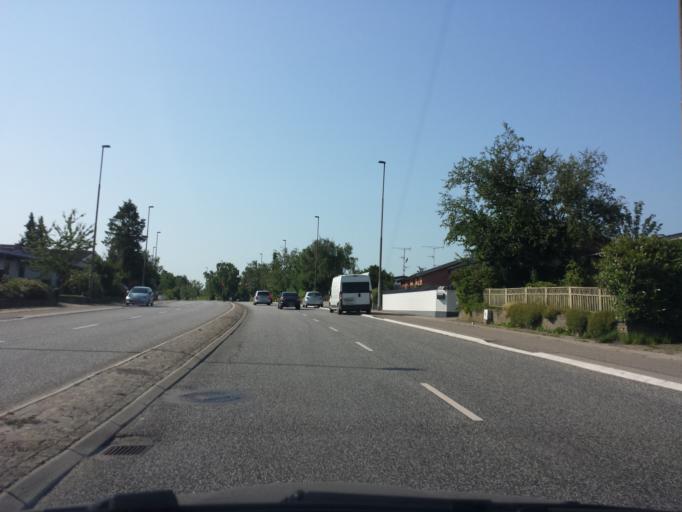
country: DK
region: Capital Region
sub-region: Ballerup Kommune
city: Ballerup
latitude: 55.7224
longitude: 12.3459
